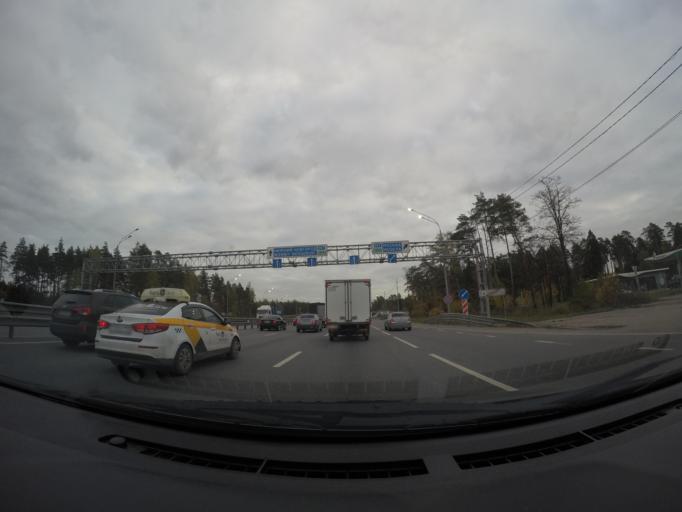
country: RU
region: Moskovskaya
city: Zarya
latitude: 55.8078
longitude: 38.0633
